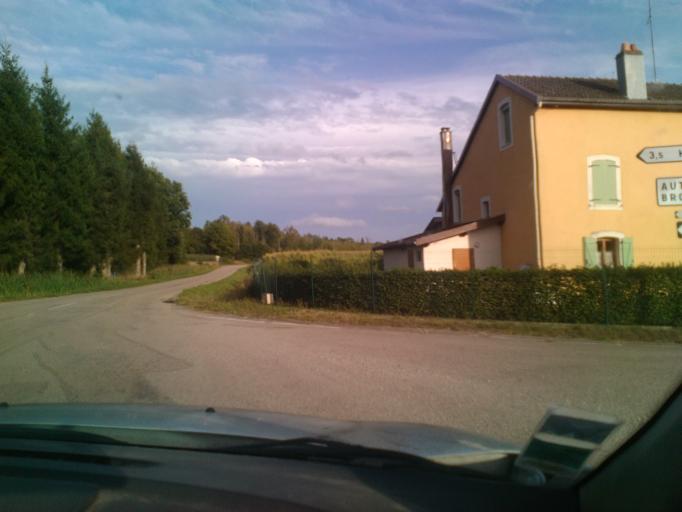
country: FR
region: Lorraine
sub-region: Departement des Vosges
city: Jeanmenil
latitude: 48.3272
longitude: 6.6782
